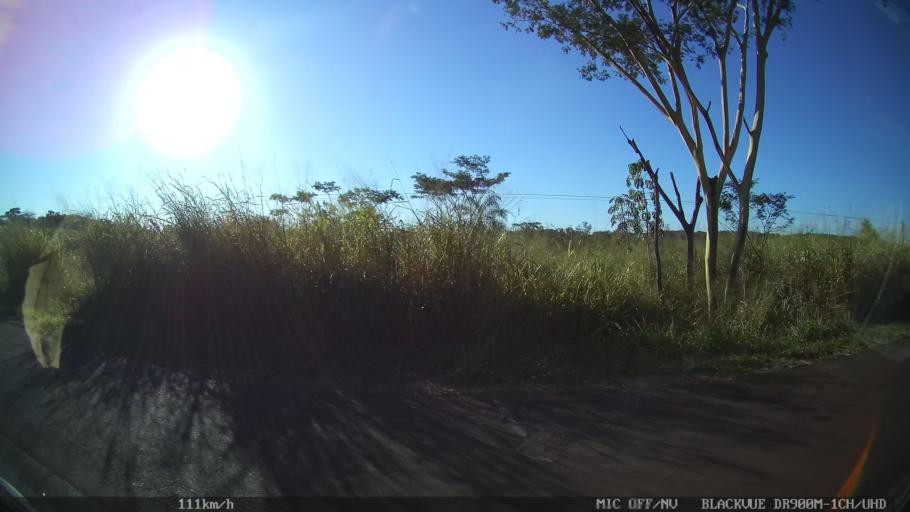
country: BR
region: Sao Paulo
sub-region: Guapiacu
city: Guapiacu
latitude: -20.7446
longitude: -49.1116
